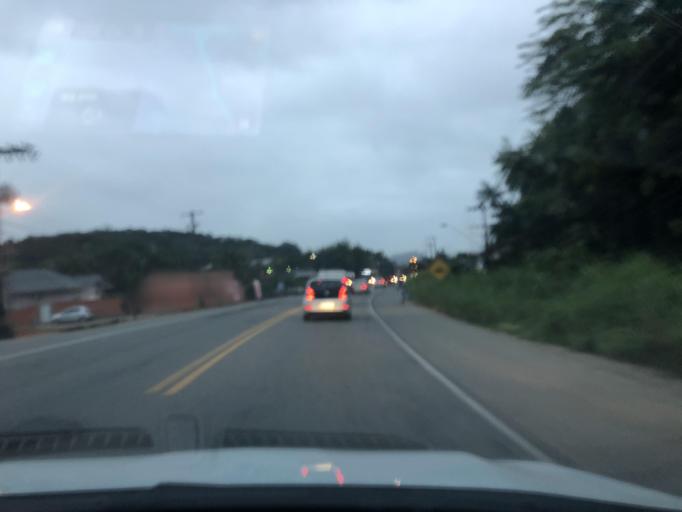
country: BR
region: Santa Catarina
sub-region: Pomerode
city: Pomerode
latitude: -26.7930
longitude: -49.0872
